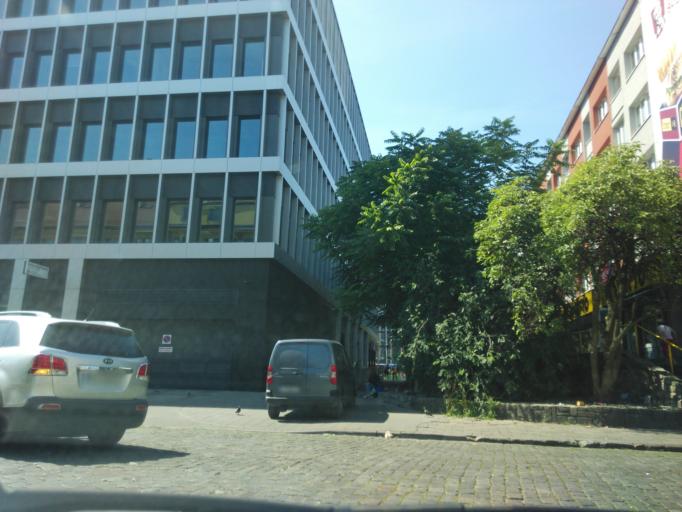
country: PL
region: West Pomeranian Voivodeship
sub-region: Szczecin
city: Szczecin
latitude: 53.4253
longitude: 14.5526
